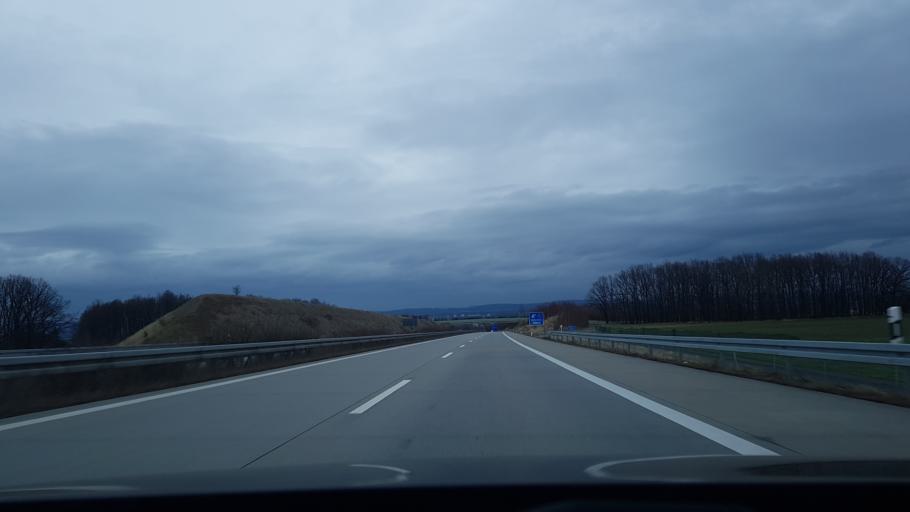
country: DE
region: Saxony
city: Liebstadt
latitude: 50.8887
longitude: 13.8818
